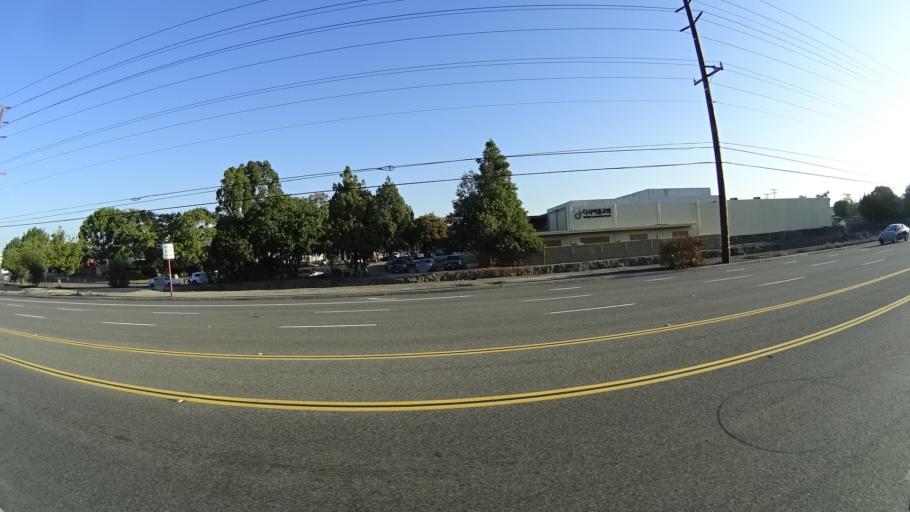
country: US
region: California
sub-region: Orange County
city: Irvine
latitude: 33.6968
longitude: -117.8591
